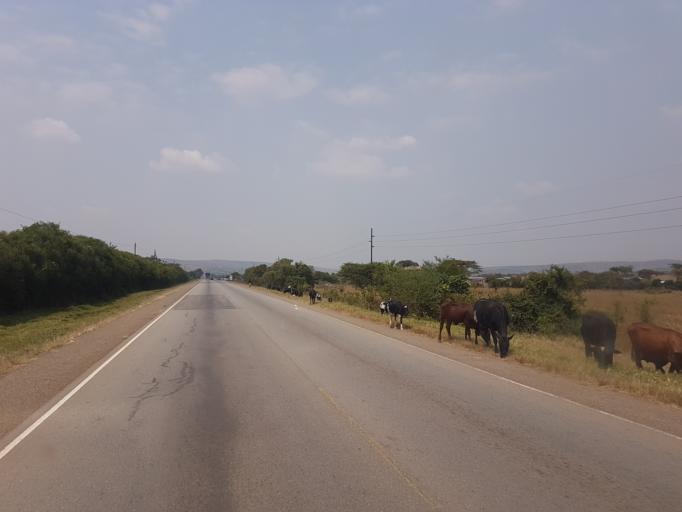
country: UG
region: Western Region
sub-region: Mbarara District
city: Mbarara
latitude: -0.5108
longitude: 30.8189
